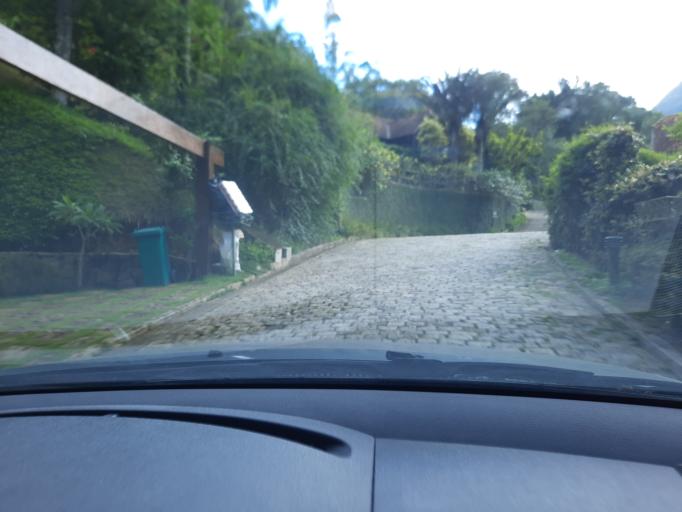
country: BR
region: Rio de Janeiro
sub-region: Petropolis
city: Petropolis
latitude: -22.4417
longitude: -43.1732
